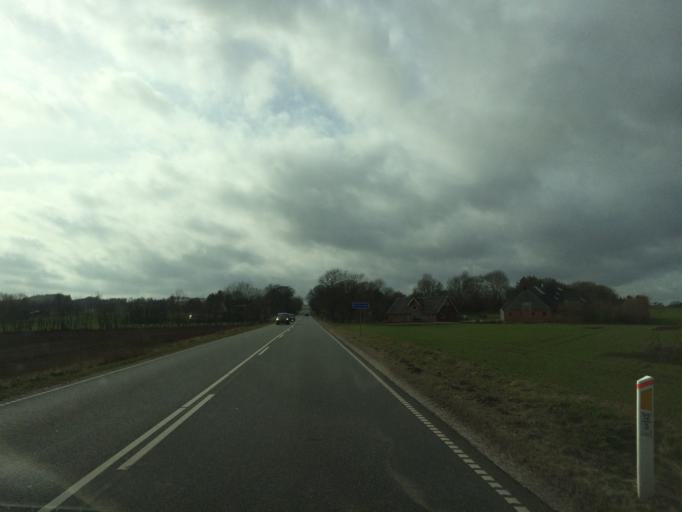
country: DK
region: Central Jutland
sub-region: Randers Kommune
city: Langa
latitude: 56.4932
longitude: 9.8505
